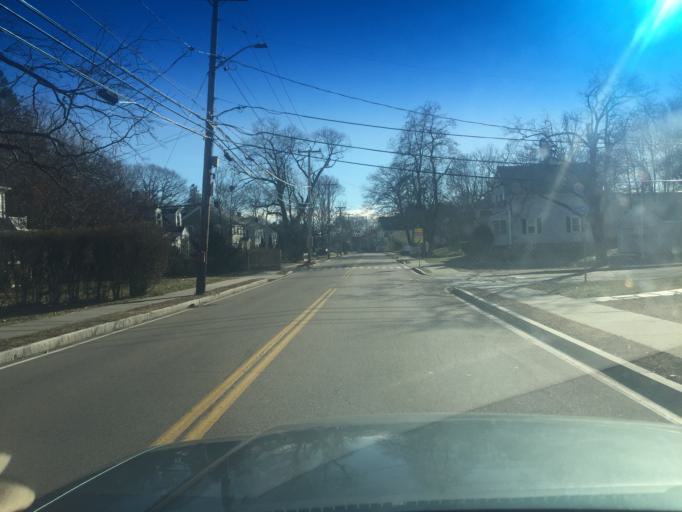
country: US
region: Massachusetts
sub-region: Norfolk County
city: Norwood
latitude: 42.2035
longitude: -71.2076
